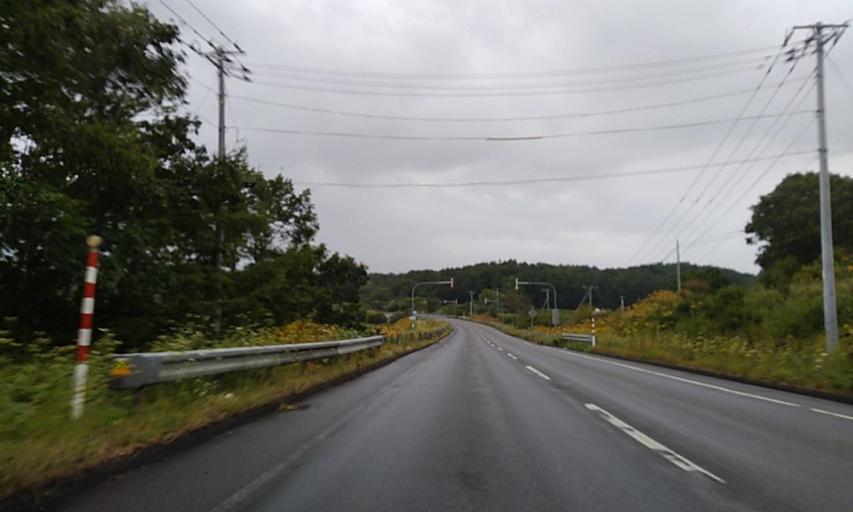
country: JP
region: Hokkaido
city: Mombetsu
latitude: 44.5026
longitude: 143.0737
